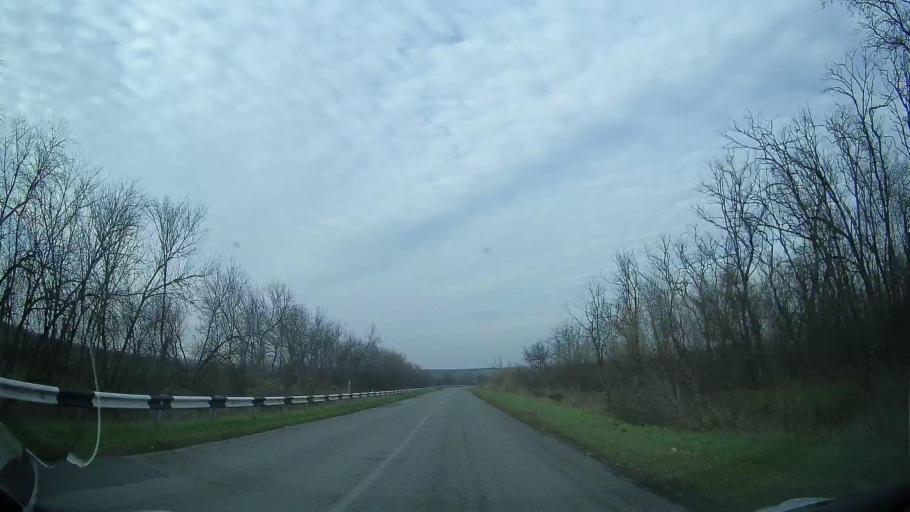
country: RU
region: Rostov
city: Zernograd
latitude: 46.8868
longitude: 40.3408
